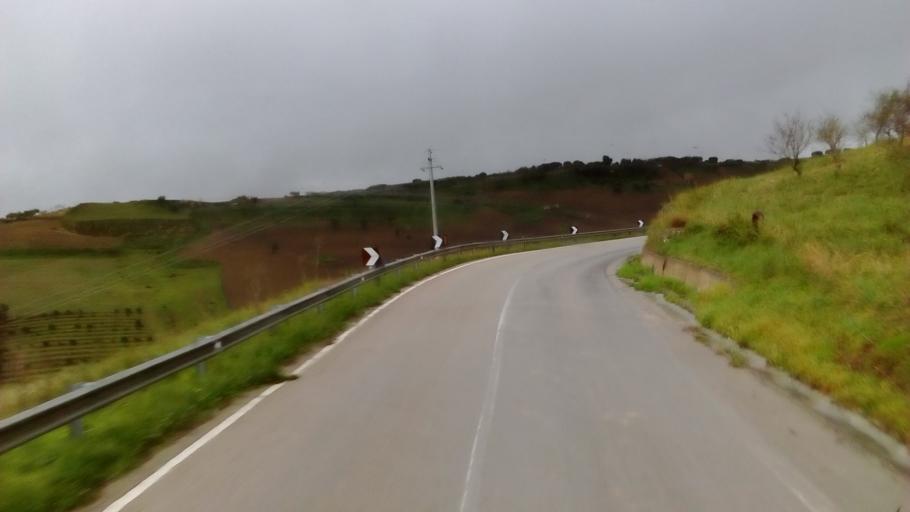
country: IT
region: Sicily
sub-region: Enna
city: Pietraperzia
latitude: 37.4411
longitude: 14.1770
